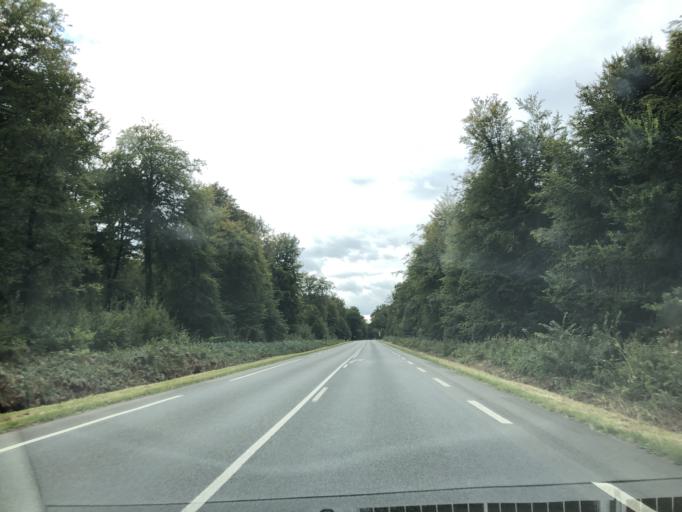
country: FR
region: Nord-Pas-de-Calais
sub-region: Departement du Pas-de-Calais
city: Hesdin
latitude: 50.3967
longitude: 2.0431
